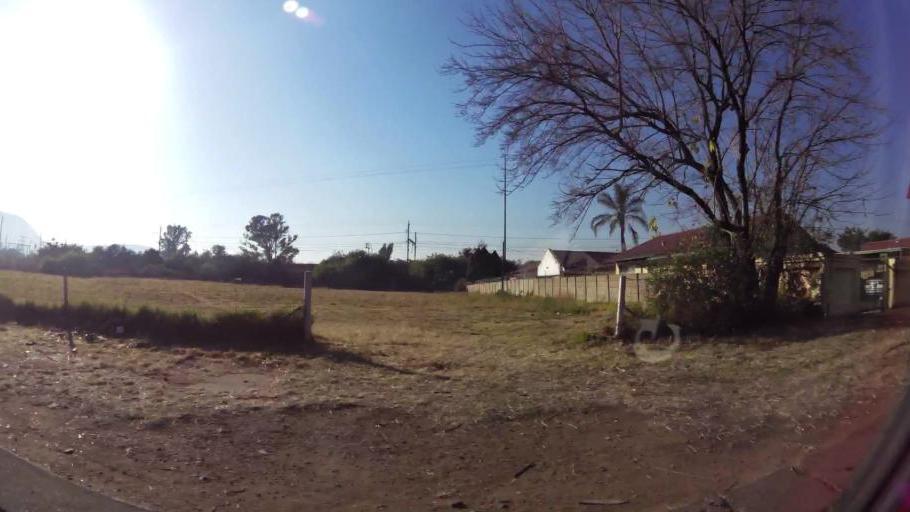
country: ZA
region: Gauteng
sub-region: City of Tshwane Metropolitan Municipality
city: Pretoria
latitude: -25.7051
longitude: 28.1678
